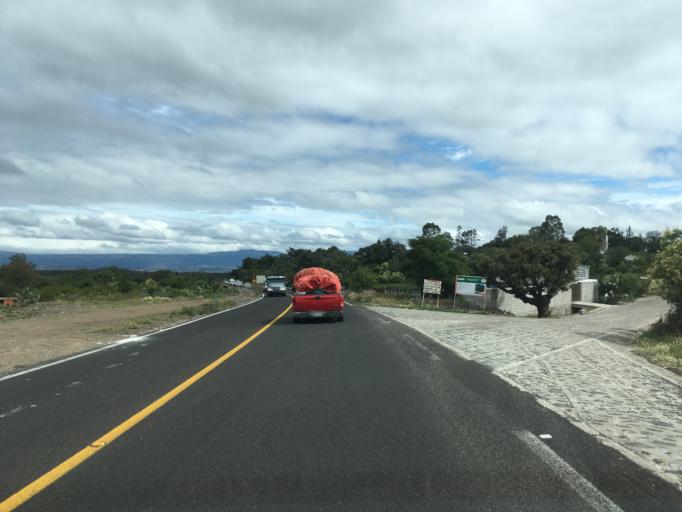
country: MX
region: Hidalgo
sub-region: Atotonilco el Grande
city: Santa Maria Amajac
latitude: 20.4074
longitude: -98.7082
